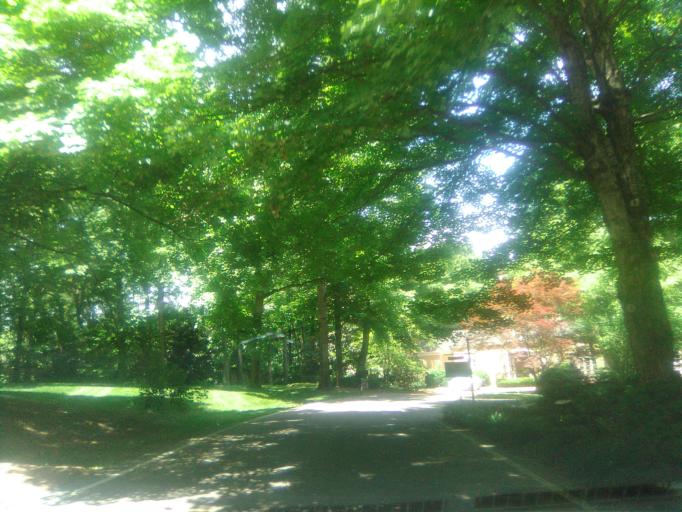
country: US
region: Tennessee
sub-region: Davidson County
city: Belle Meade
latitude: 36.1169
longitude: -86.8454
